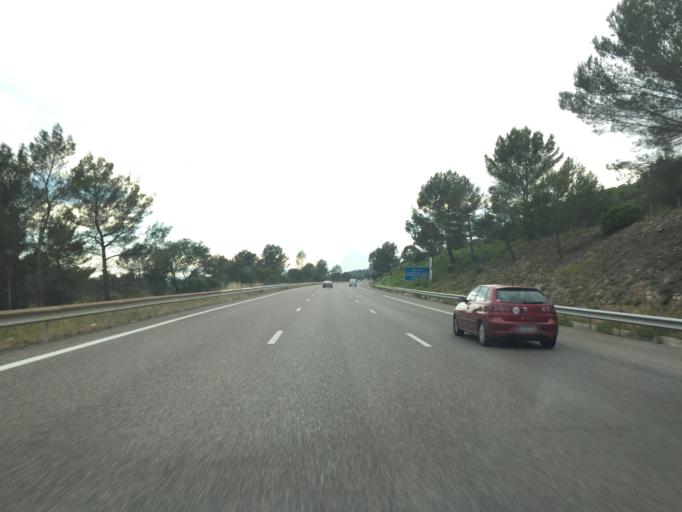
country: FR
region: Provence-Alpes-Cote d'Azur
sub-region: Departement du Var
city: La Celle
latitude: 43.4189
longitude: 6.0232
